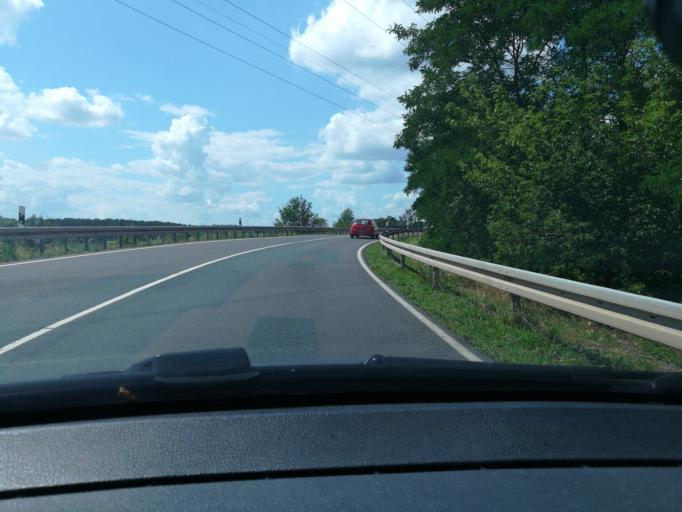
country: DE
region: Saxony-Anhalt
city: Zielitz
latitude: 52.2855
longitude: 11.6753
